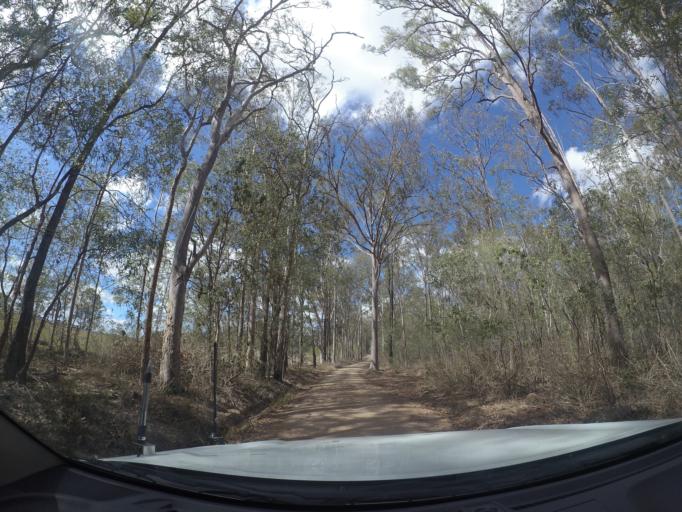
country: AU
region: Queensland
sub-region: Logan
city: North Maclean
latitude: -27.8227
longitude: 152.9692
